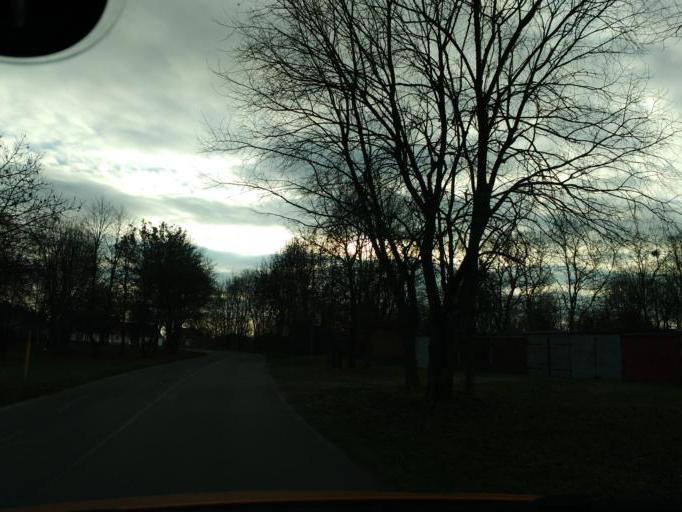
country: DE
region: Brandenburg
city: Wriezen
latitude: 52.7246
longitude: 14.1396
